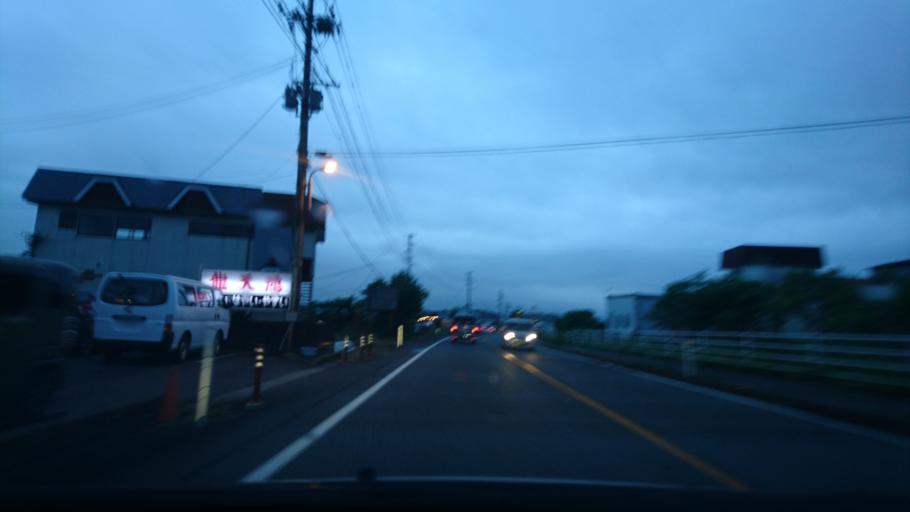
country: JP
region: Iwate
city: Ichinoseki
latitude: 38.8079
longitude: 141.0753
